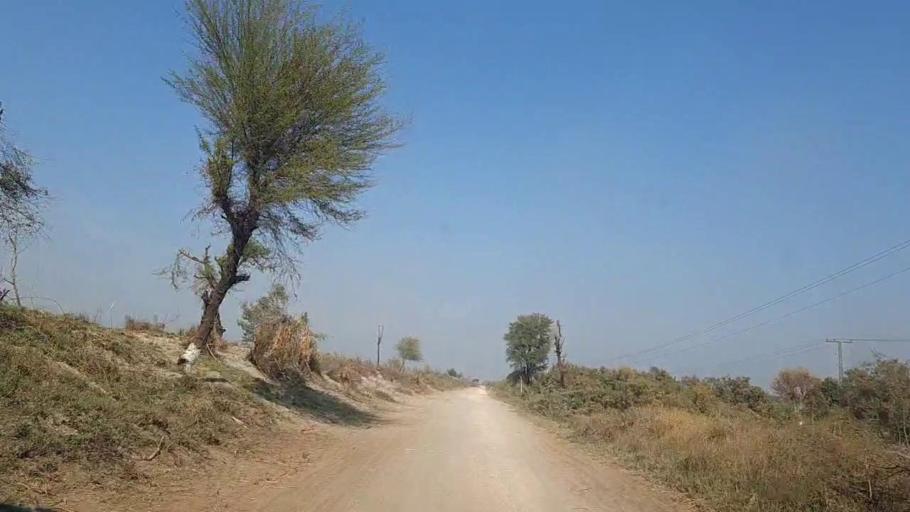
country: PK
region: Sindh
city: Sakrand
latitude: 26.0648
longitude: 68.3493
